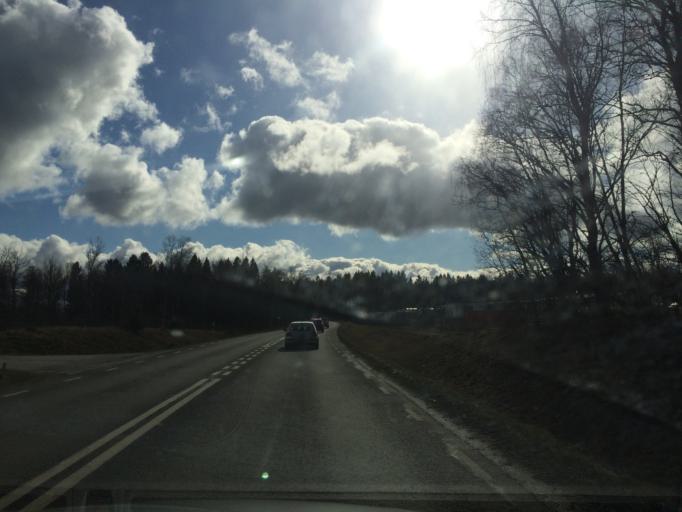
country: SE
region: Vaestra Goetaland
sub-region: Skara Kommun
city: Skara
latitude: 58.3350
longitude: 13.4362
